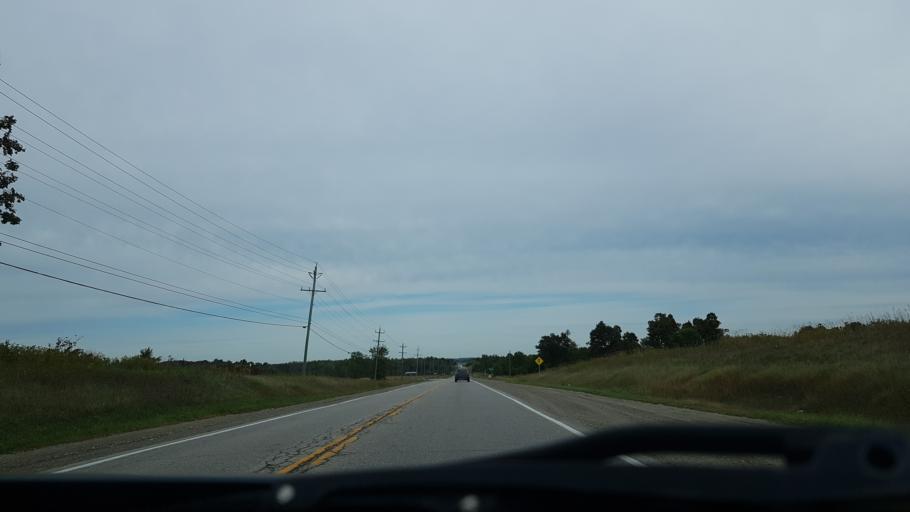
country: CA
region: Ontario
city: Orangeville
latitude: 43.7892
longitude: -80.0741
